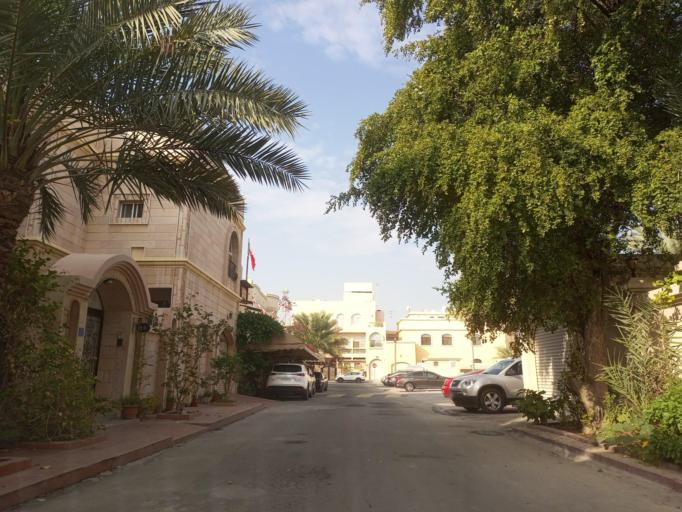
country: BH
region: Muharraq
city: Al Hadd
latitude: 26.2494
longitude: 50.6428
